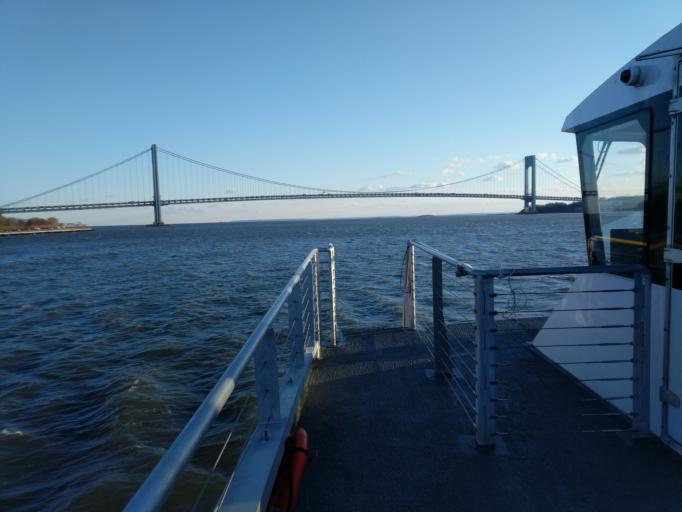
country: US
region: New York
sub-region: Kings County
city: Bensonhurst
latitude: 40.6213
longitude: -74.0441
